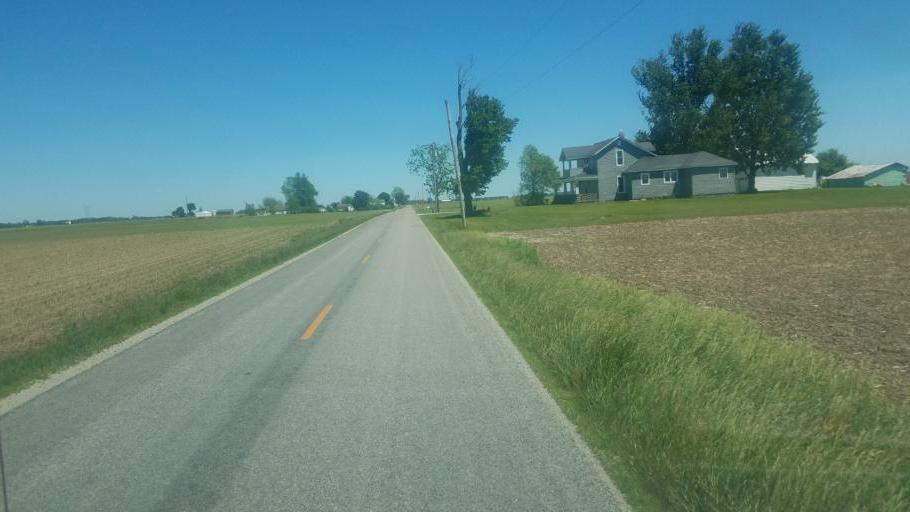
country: US
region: Ohio
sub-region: Shelby County
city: Sidney
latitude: 40.2106
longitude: -84.1087
